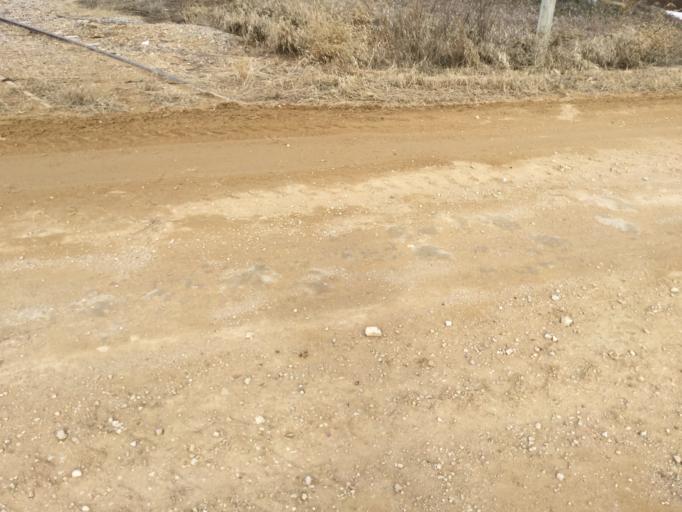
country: US
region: Kansas
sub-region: Lincoln County
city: Lincoln
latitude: 39.1612
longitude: -98.3618
